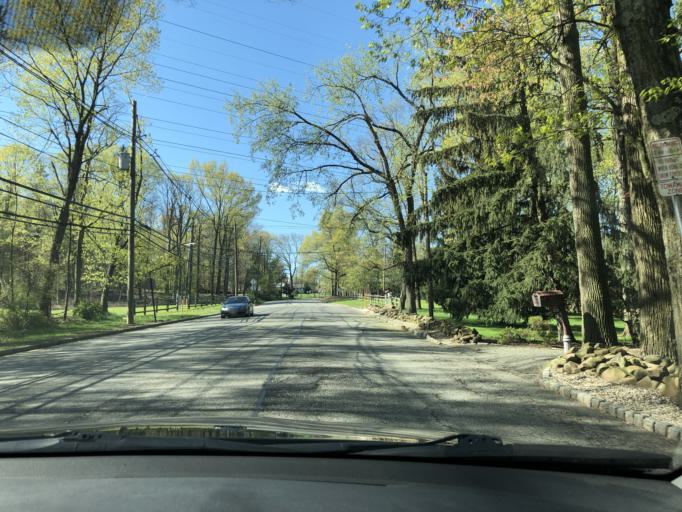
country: US
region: New Jersey
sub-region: Essex County
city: North Caldwell
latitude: 40.8614
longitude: -74.2576
